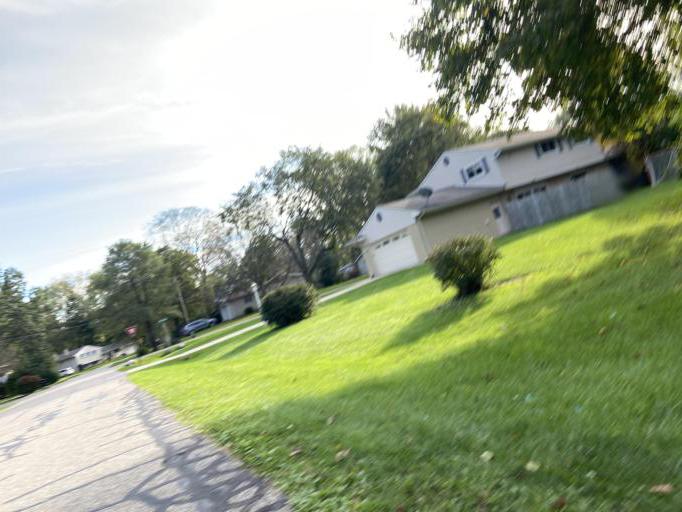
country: US
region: Michigan
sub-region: Oakland County
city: Farmington Hills
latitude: 42.5121
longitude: -83.3684
